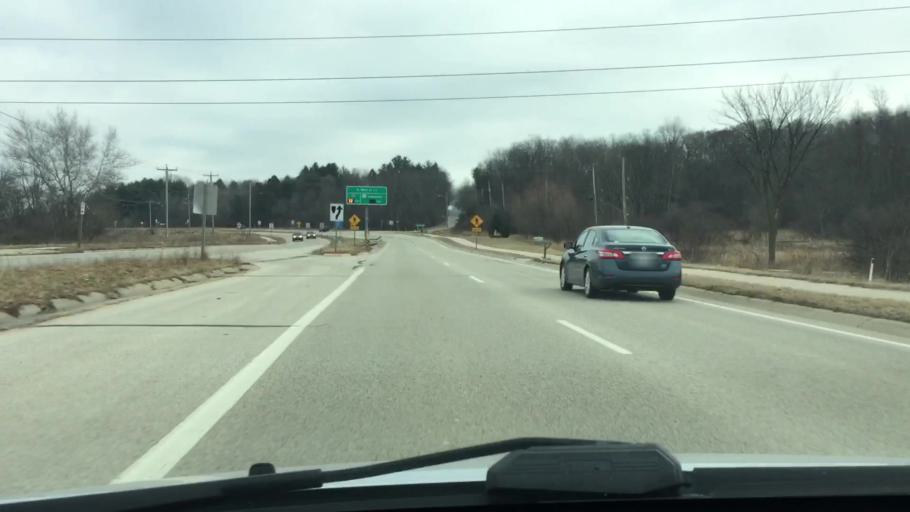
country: US
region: Wisconsin
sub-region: Waukesha County
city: Waukesha
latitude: 43.0138
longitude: -88.1752
